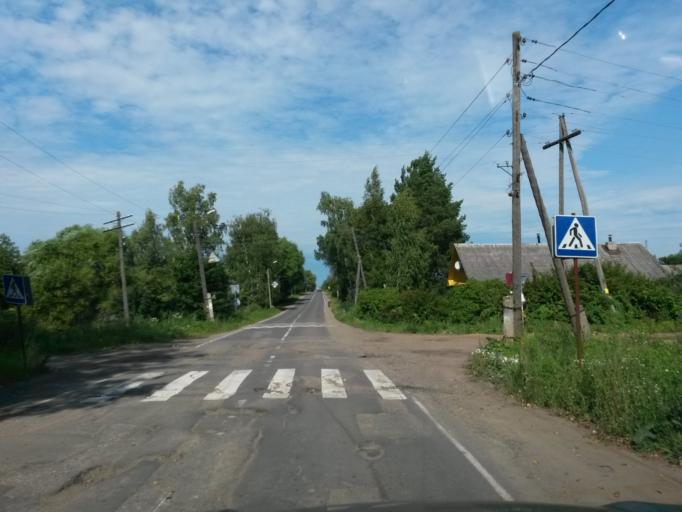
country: RU
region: Jaroslavl
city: Tutayev
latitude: 57.8871
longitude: 39.5404
